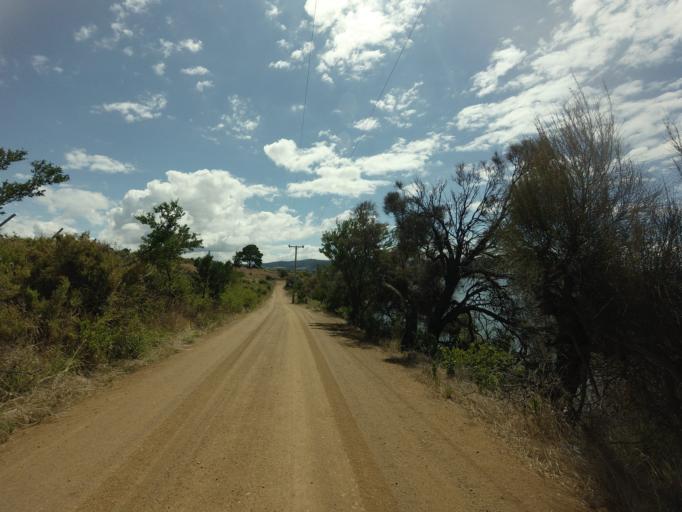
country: AU
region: Tasmania
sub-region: Clarence
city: Rokeby
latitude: -42.9195
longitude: 147.4337
